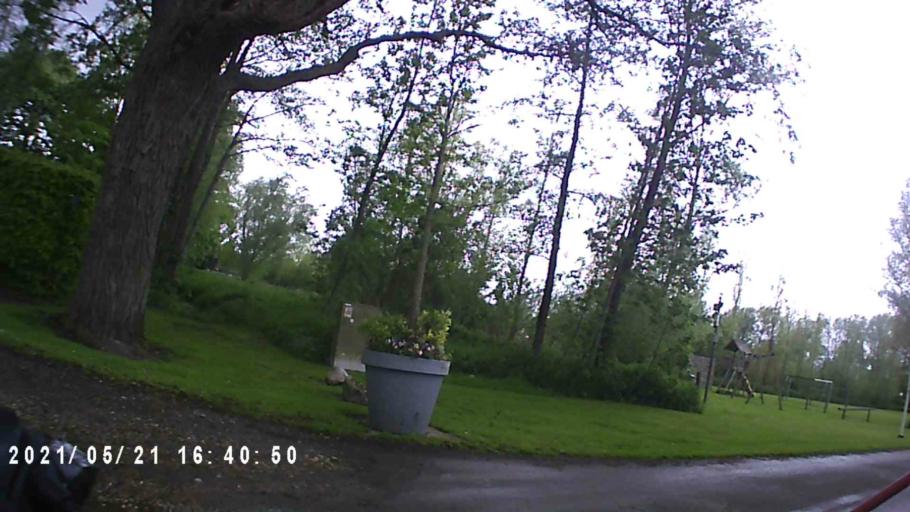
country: NL
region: Groningen
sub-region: Gemeente Zuidhorn
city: Aduard
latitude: 53.1932
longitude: 6.4516
